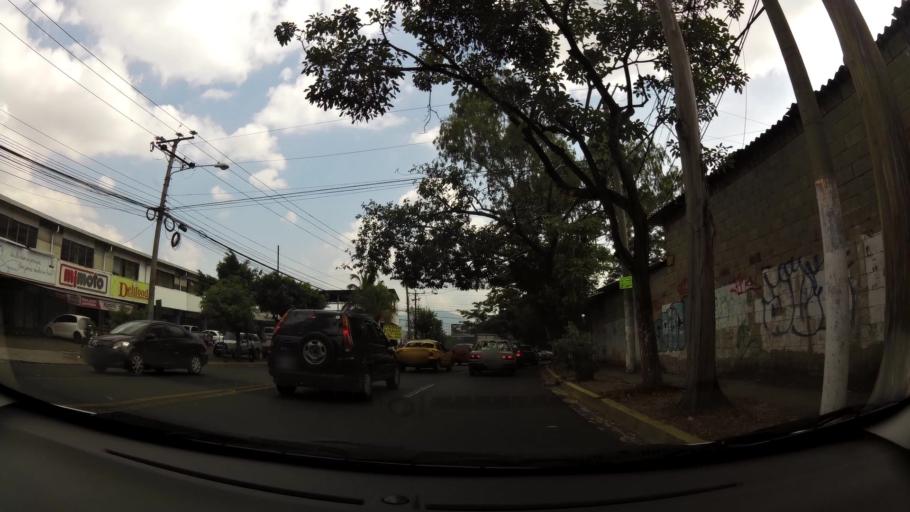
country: SV
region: San Salvador
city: Mejicanos
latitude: 13.7068
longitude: -89.2257
